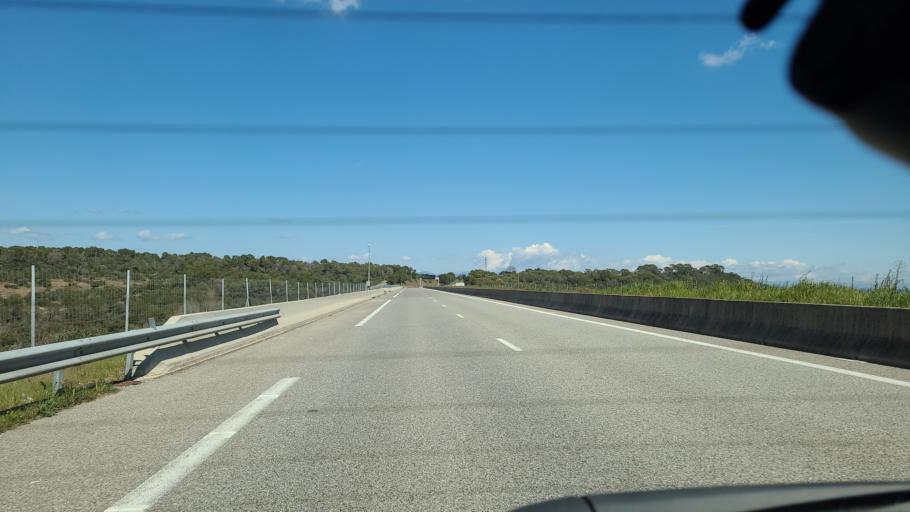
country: FR
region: Provence-Alpes-Cote d'Azur
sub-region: Departement du Var
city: Le Cannet-des-Maures
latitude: 43.3695
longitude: 6.3441
